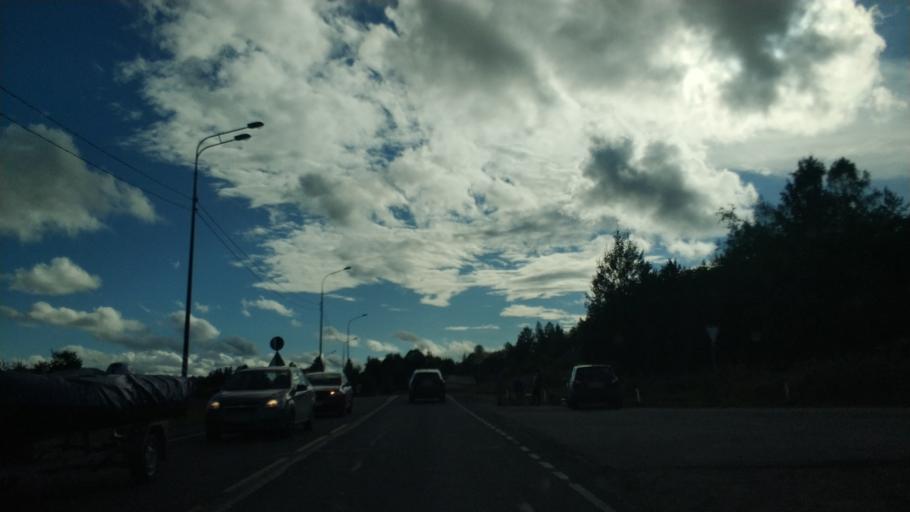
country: RU
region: Republic of Karelia
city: Lakhdenpokh'ya
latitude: 61.5554
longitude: 30.3234
